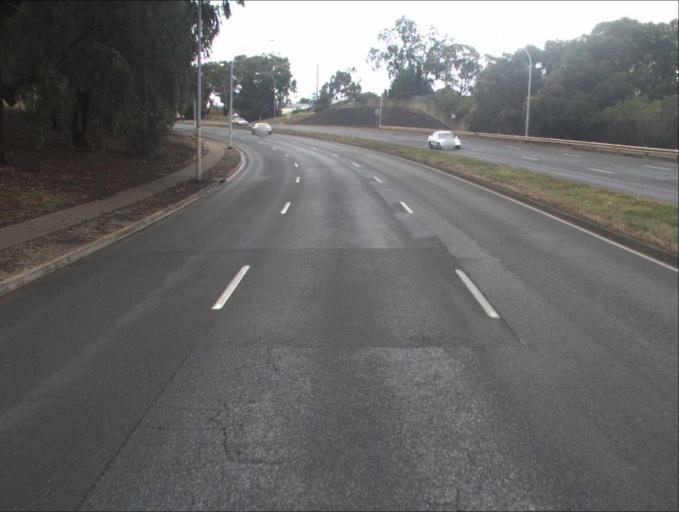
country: AU
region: South Australia
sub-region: Campbelltown
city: Paradise
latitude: -34.8634
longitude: 138.6615
